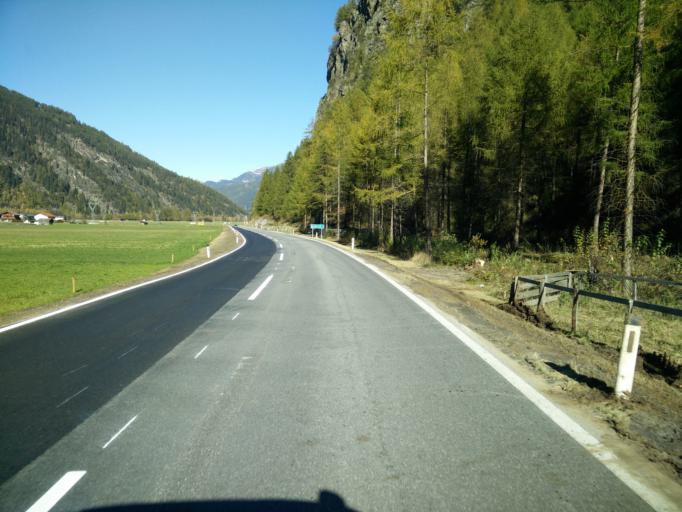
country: AT
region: Tyrol
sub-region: Politischer Bezirk Imst
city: Umhausen
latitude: 47.0535
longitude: 10.9663
